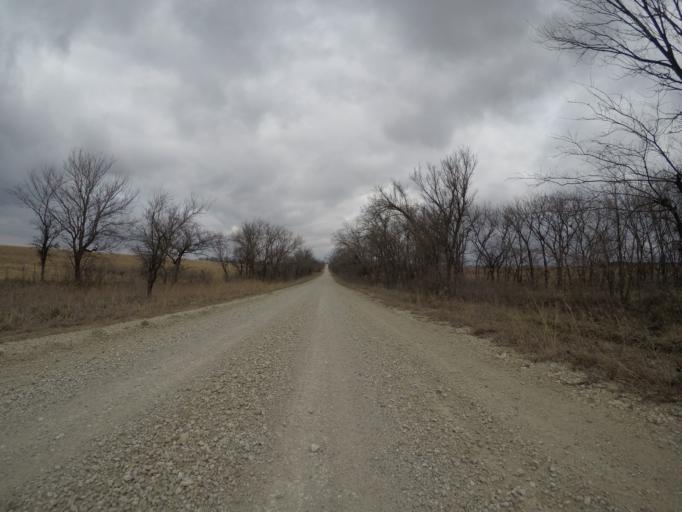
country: US
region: Kansas
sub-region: Morris County
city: Council Grove
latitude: 38.7309
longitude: -96.2796
